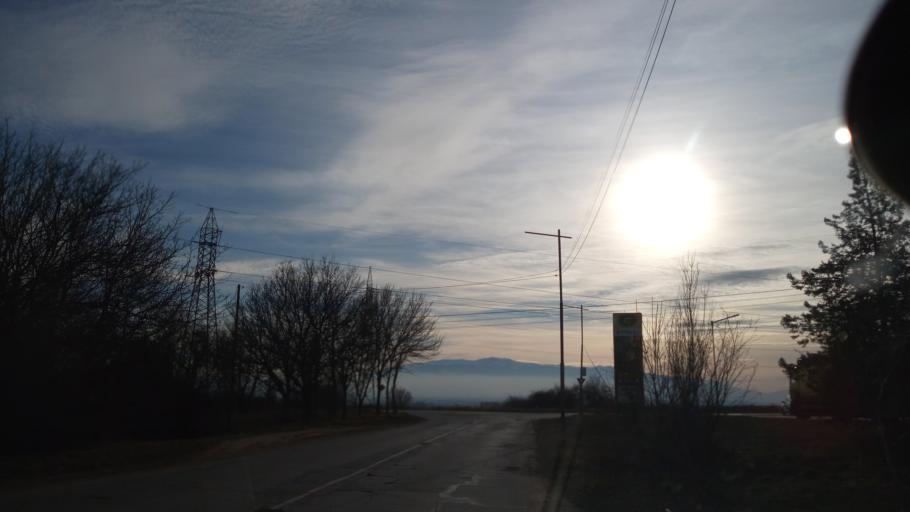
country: BG
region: Sofia-Capital
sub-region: Stolichna Obshtina
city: Bukhovo
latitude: 42.7553
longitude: 23.5591
